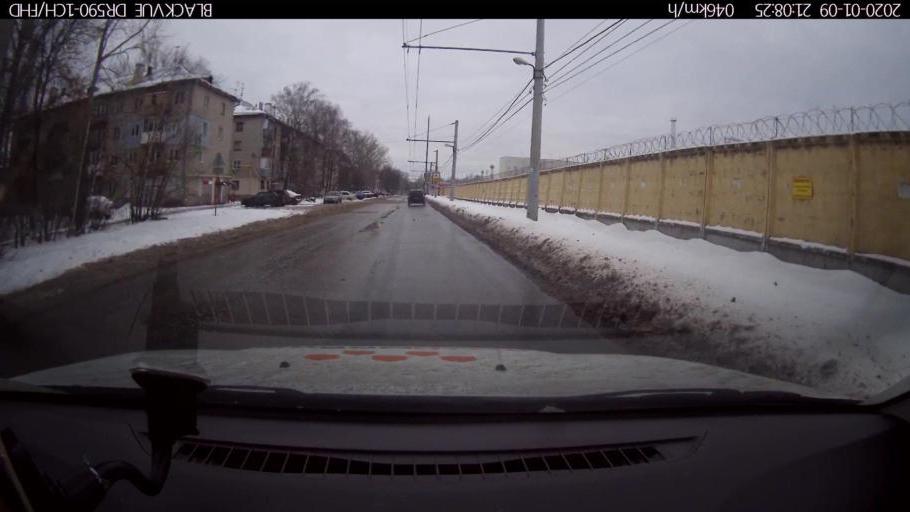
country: RU
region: Nizjnij Novgorod
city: Gorbatovka
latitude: 56.2940
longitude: 43.8652
